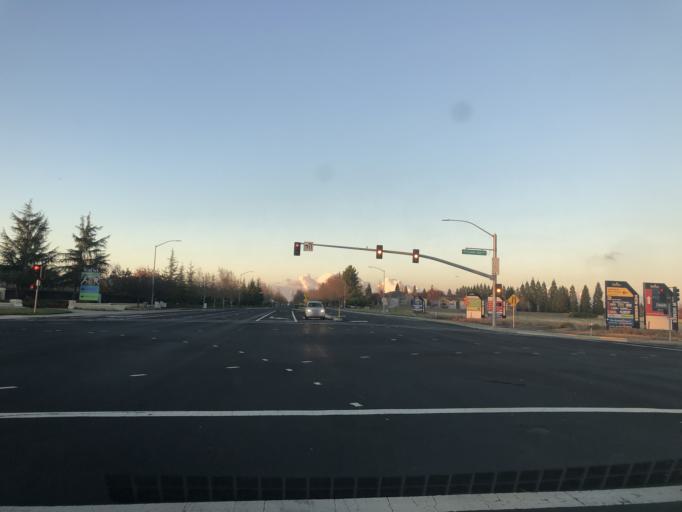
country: US
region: California
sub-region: Sacramento County
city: Antelope
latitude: 38.7660
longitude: -121.3587
